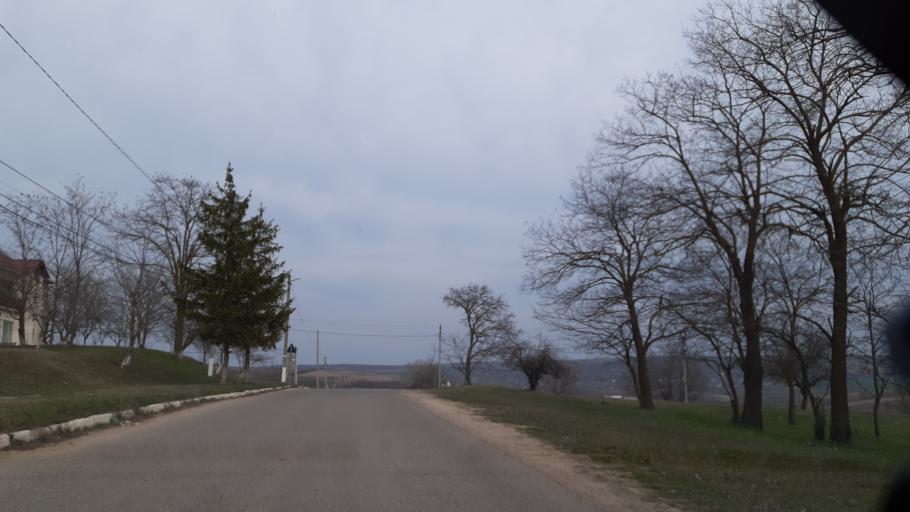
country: MD
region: Soldanesti
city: Soldanesti
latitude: 47.6842
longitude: 28.7707
